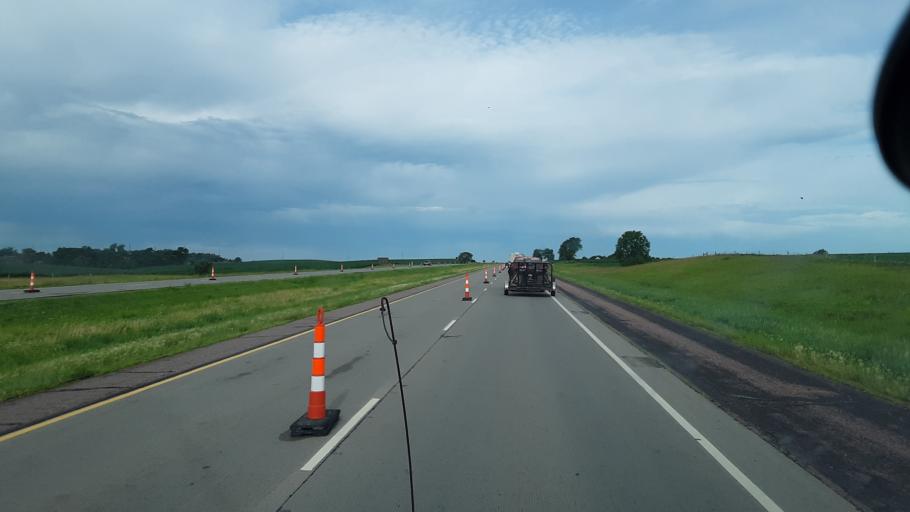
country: US
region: South Dakota
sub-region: Minnehaha County
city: Crooks
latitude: 43.6087
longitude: -96.8563
